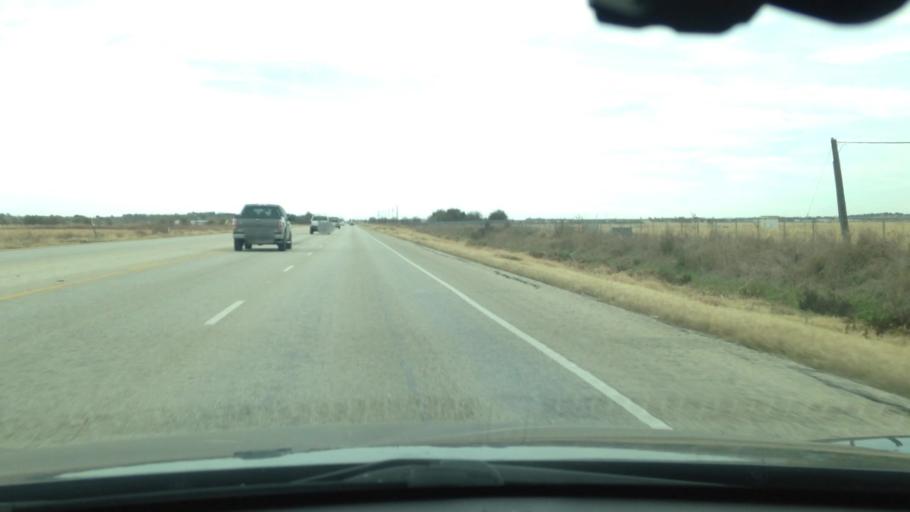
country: US
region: Texas
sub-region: Caldwell County
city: Martindale
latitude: 29.8977
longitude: -97.8753
